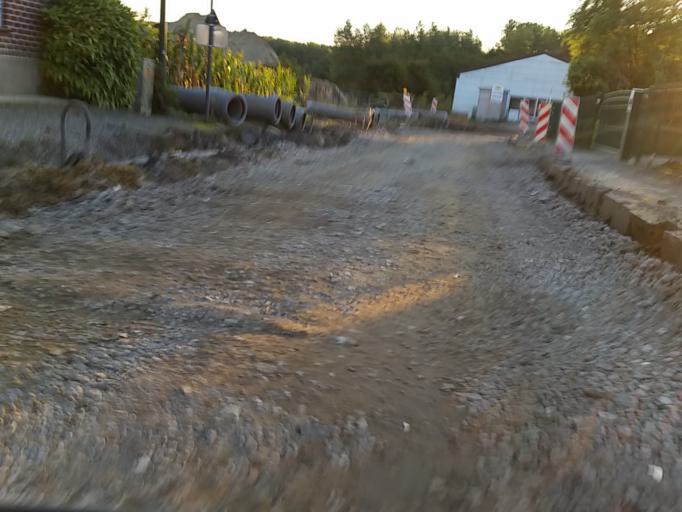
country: BE
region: Flanders
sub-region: Provincie Vlaams-Brabant
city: Kampenhout
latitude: 50.9500
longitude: 4.5466
